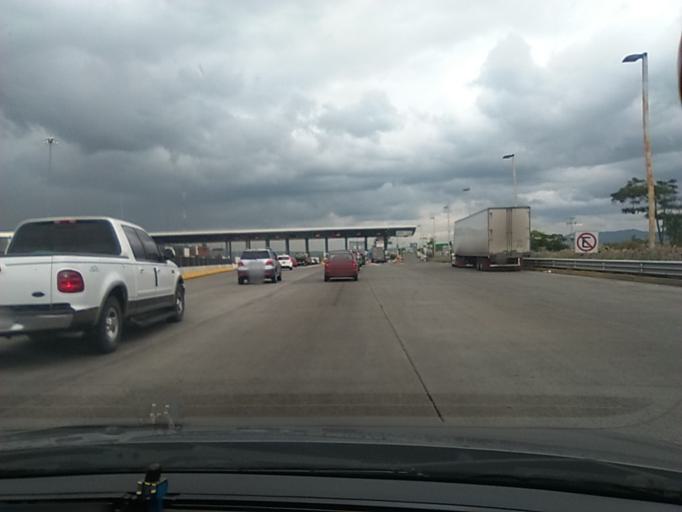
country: MX
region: Jalisco
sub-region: Tonala
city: Mismaloya (Fraccionamiento Pedregal de Santa Martha)
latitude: 20.6040
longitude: -103.1404
